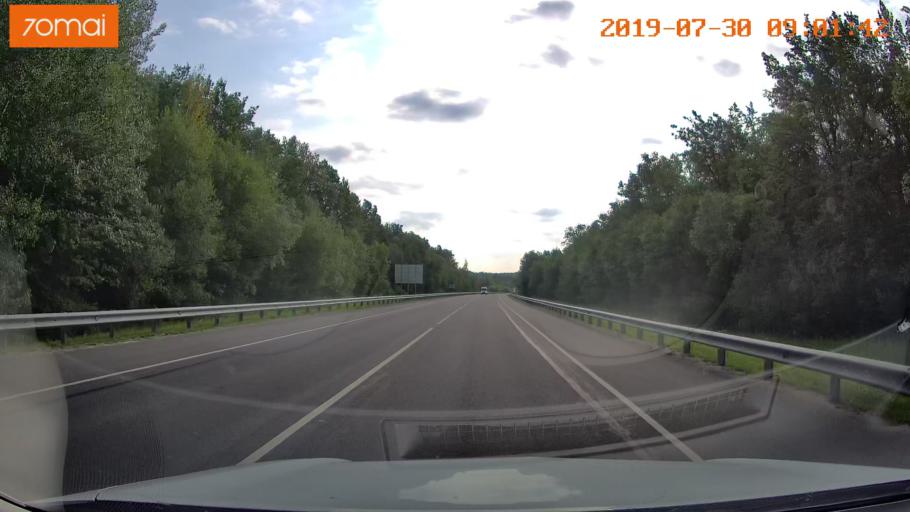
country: RU
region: Kaliningrad
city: Gusev
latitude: 54.6174
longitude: 22.2126
